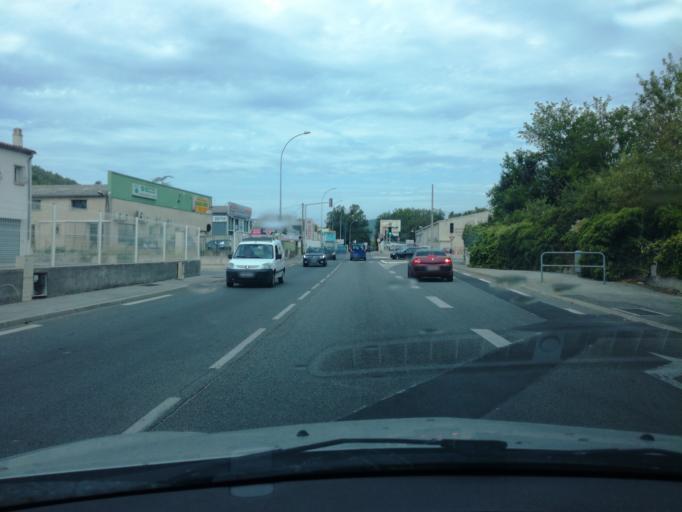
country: FR
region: Provence-Alpes-Cote d'Azur
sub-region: Departement du Var
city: Draguignan
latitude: 43.5223
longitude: 6.4653
